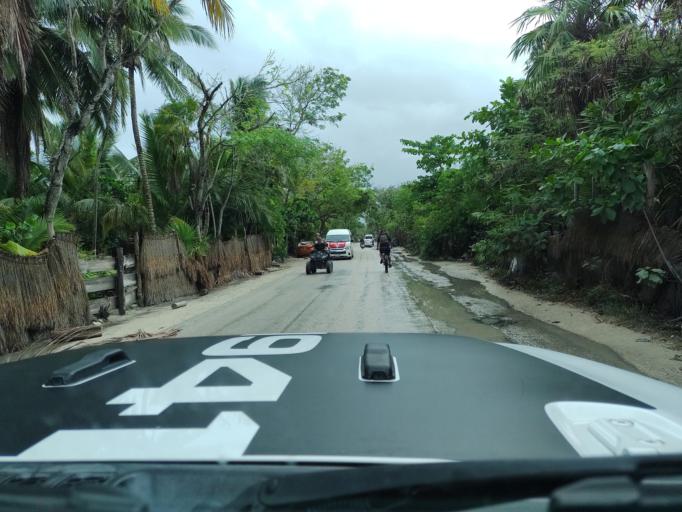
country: MX
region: Quintana Roo
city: Tulum
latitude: 20.1626
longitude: -87.4544
